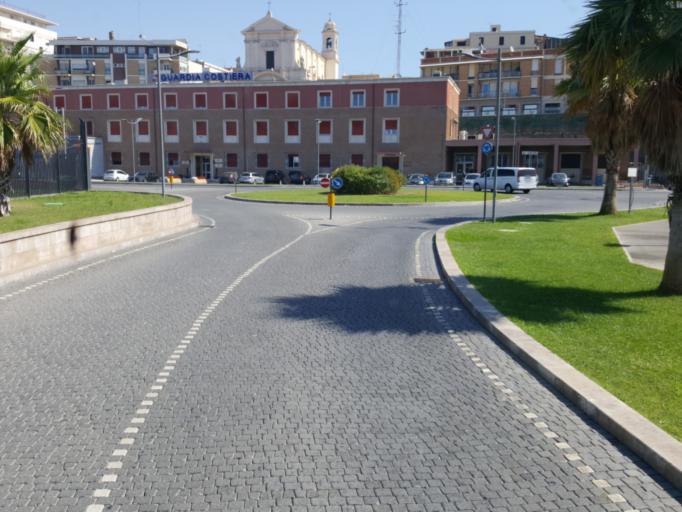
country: IT
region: Latium
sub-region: Citta metropolitana di Roma Capitale
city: Civitavecchia
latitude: 42.0912
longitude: 11.7905
